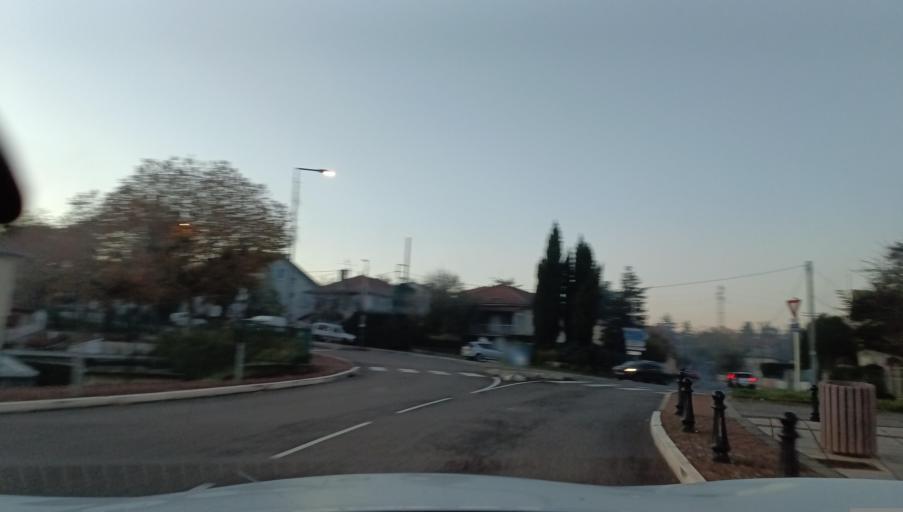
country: FR
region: Rhone-Alpes
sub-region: Departement de l'Isere
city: Chasse-sur-Rhone
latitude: 45.5809
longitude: 4.8046
